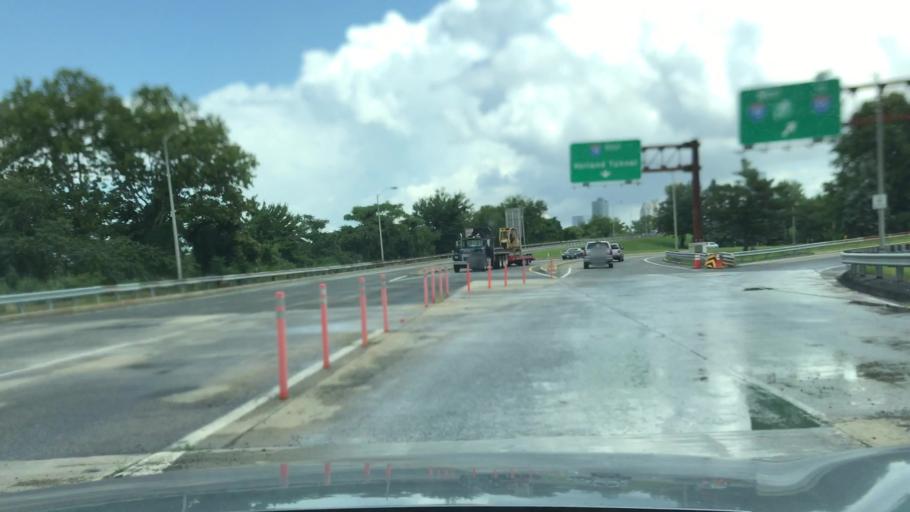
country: US
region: New Jersey
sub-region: Hudson County
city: Jersey City
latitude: 40.7024
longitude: -74.0690
